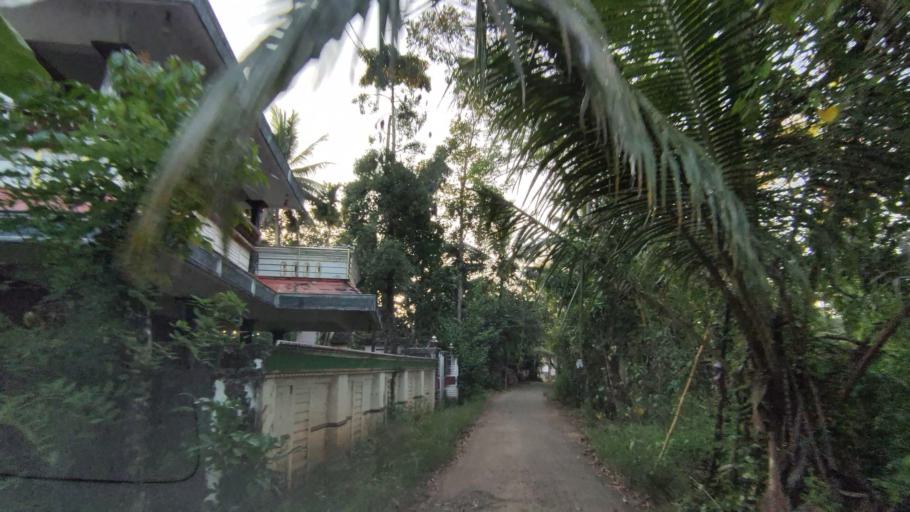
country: IN
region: Kerala
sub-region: Kottayam
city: Kottayam
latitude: 9.6327
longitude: 76.4798
